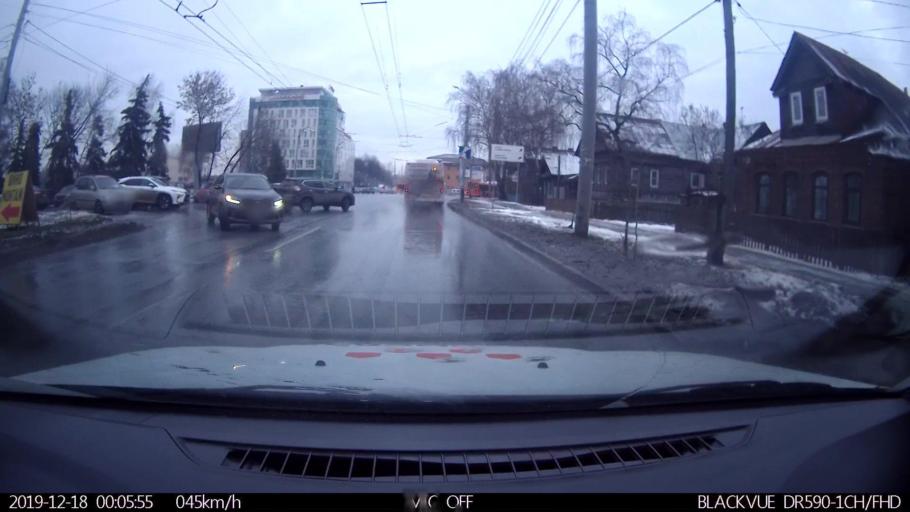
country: RU
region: Nizjnij Novgorod
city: Neklyudovo
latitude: 56.3617
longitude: 43.8610
